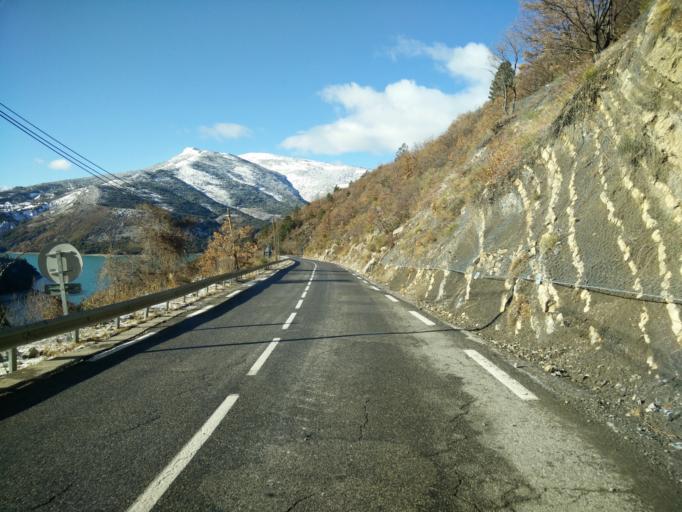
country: FR
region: Provence-Alpes-Cote d'Azur
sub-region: Departement des Alpes-de-Haute-Provence
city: Castellane
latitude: 43.9141
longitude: 6.5551
